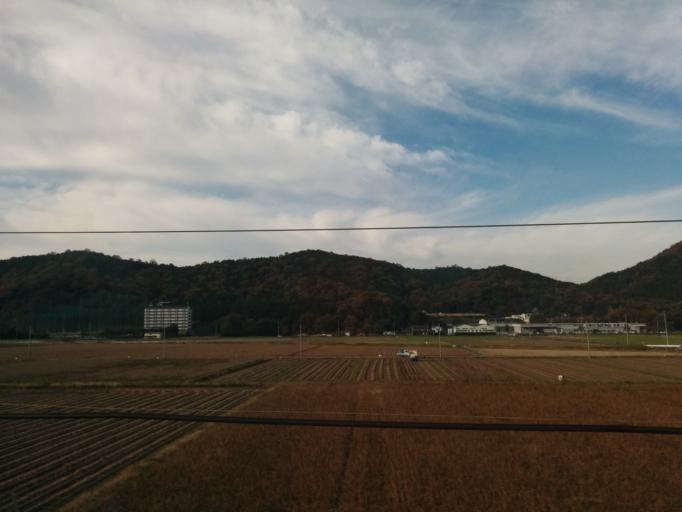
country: JP
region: Shiga Prefecture
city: Youkaichi
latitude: 35.1295
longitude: 136.1558
